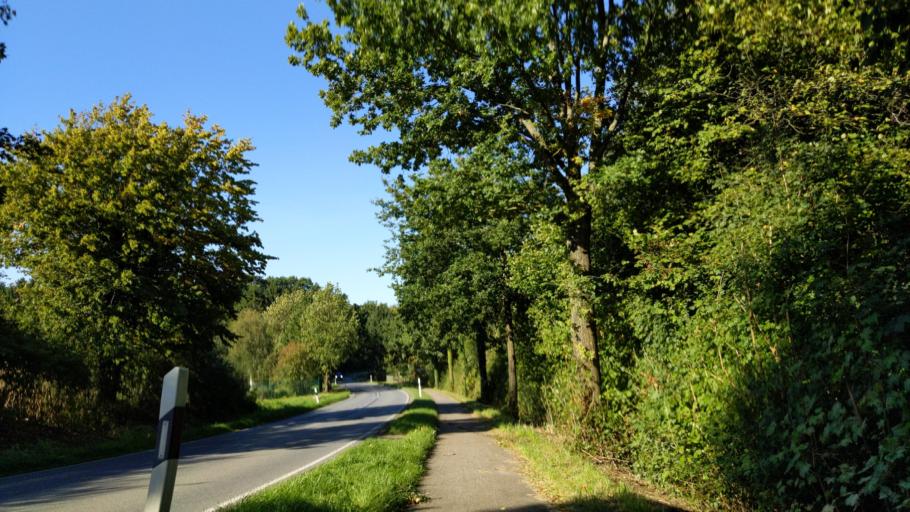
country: DE
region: Schleswig-Holstein
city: Ahrensbok
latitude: 53.9963
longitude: 10.5784
